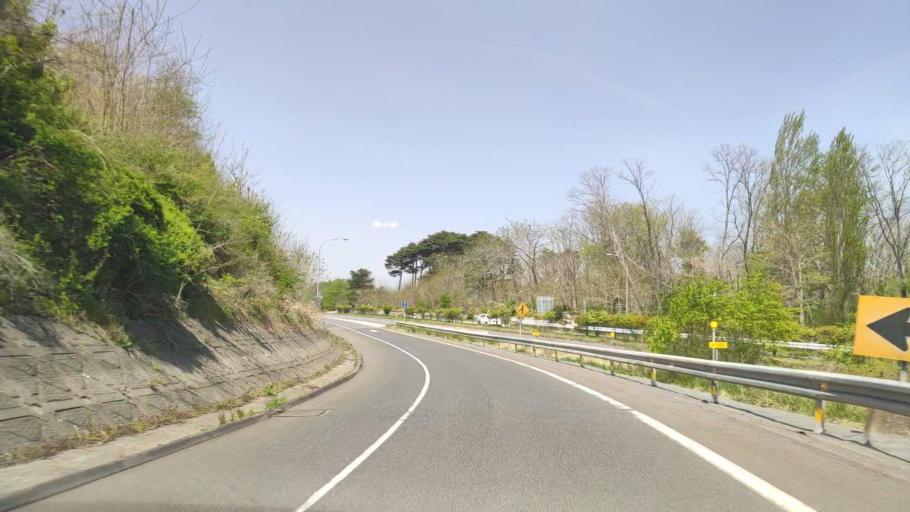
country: JP
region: Aomori
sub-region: Hachinohe Shi
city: Uchimaru
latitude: 40.4945
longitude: 141.4642
